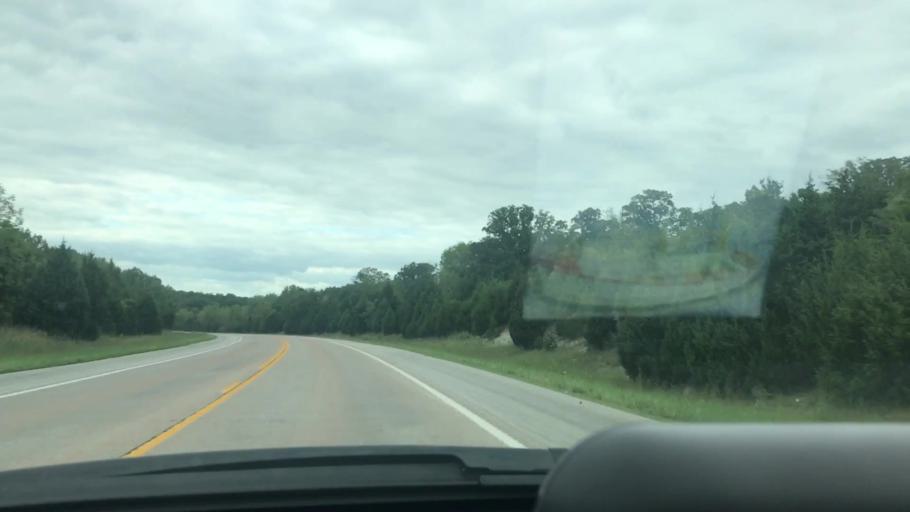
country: US
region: Missouri
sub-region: Benton County
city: Warsaw
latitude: 38.2034
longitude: -93.3263
